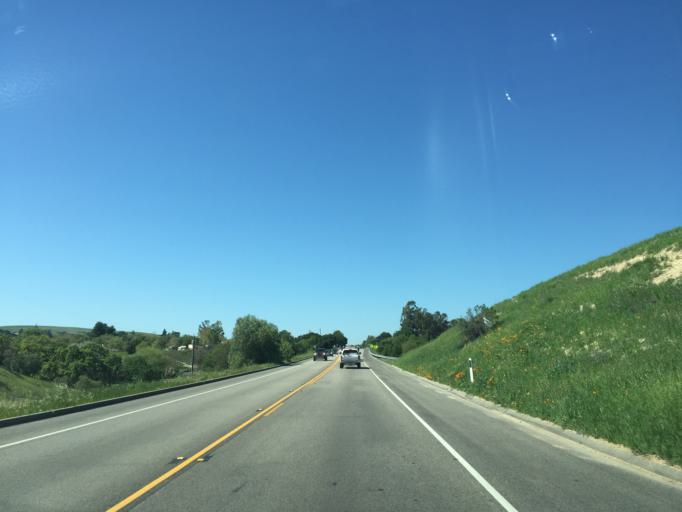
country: US
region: California
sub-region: Santa Barbara County
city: Los Olivos
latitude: 34.6629
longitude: -120.1066
